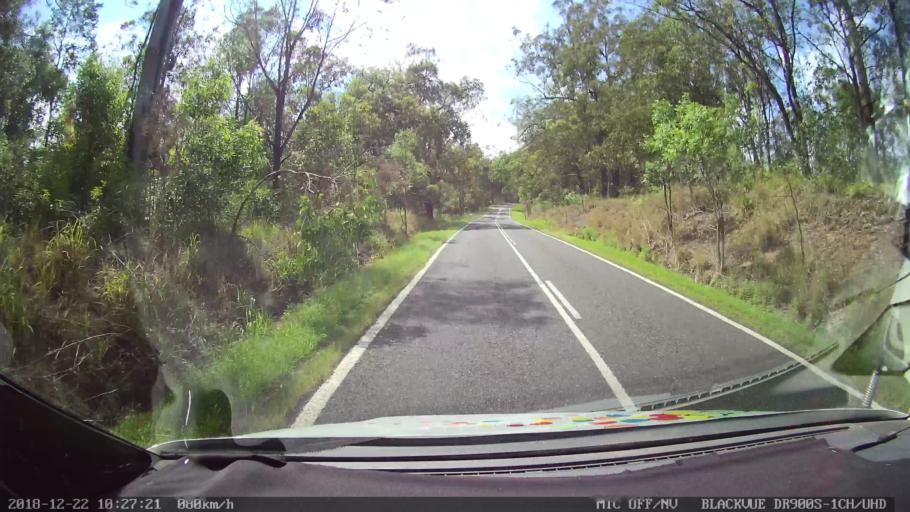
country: AU
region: New South Wales
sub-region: Clarence Valley
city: Gordon
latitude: -29.5951
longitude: 152.5813
